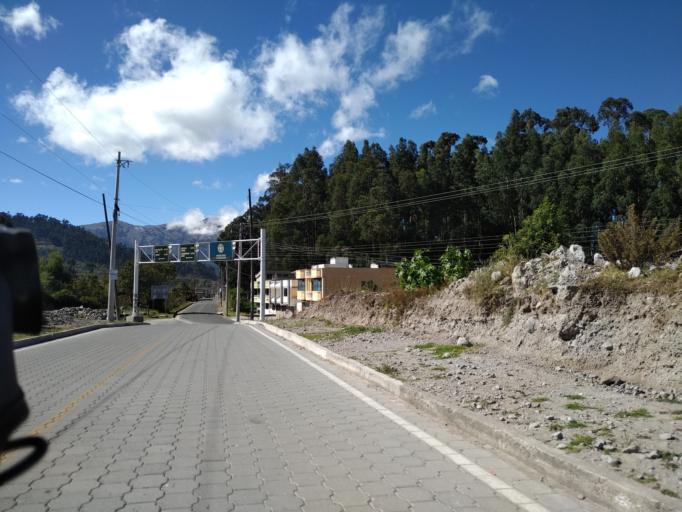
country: EC
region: Imbabura
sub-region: Canton Otavalo
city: Otavalo
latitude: 0.2202
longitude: -78.2201
